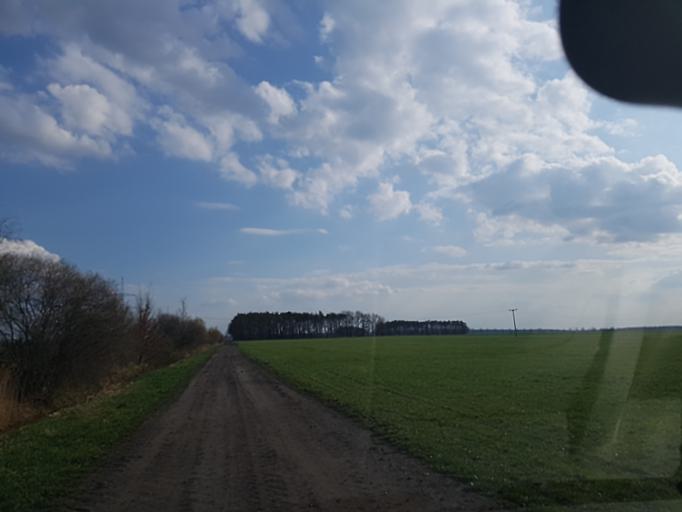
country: DE
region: Brandenburg
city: Schonborn
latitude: 51.6068
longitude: 13.5267
